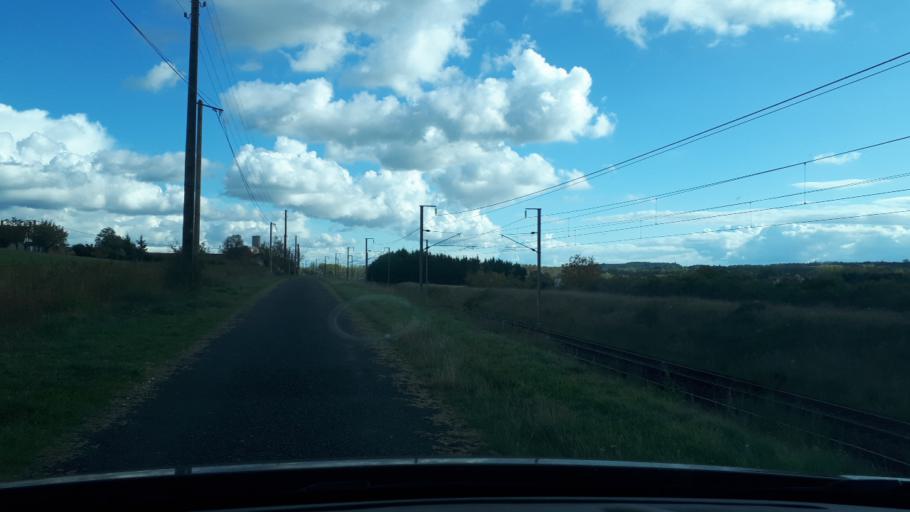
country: FR
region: Centre
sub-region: Departement du Loir-et-Cher
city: Mareuil-sur-Cher
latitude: 47.3024
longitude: 1.3517
